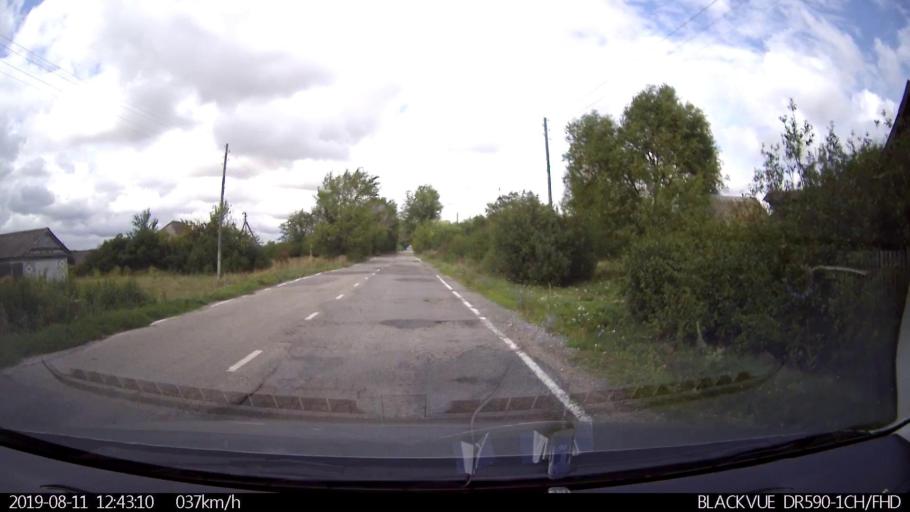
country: RU
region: Ulyanovsk
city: Ignatovka
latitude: 53.8498
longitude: 47.7447
